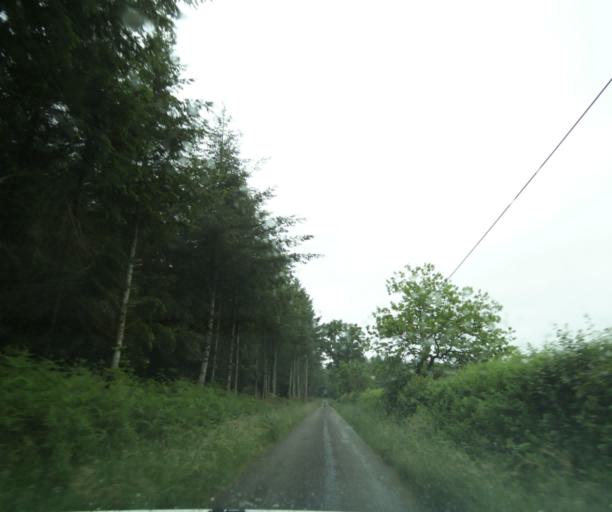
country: FR
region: Bourgogne
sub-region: Departement de Saone-et-Loire
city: La Clayette
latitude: 46.3684
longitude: 4.3670
